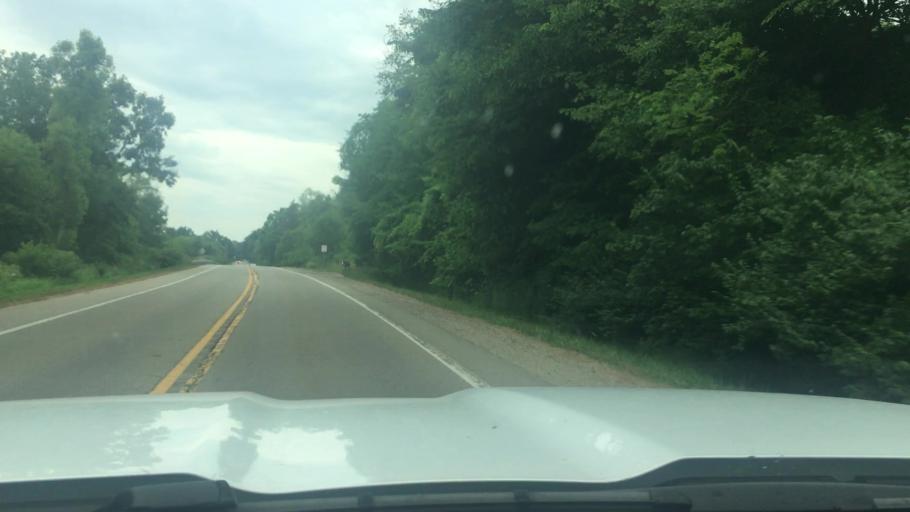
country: US
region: Michigan
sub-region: Ionia County
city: Saranac
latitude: 42.9626
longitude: -85.1555
